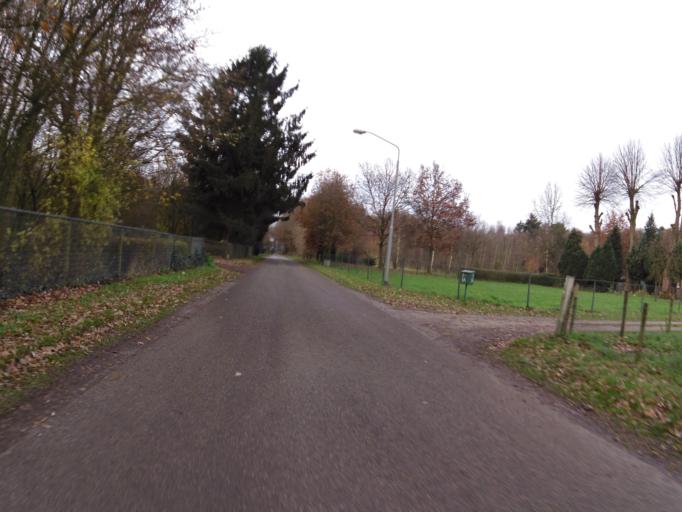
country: NL
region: North Brabant
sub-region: Gemeente Oss
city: Berghem
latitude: 51.7393
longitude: 5.5903
